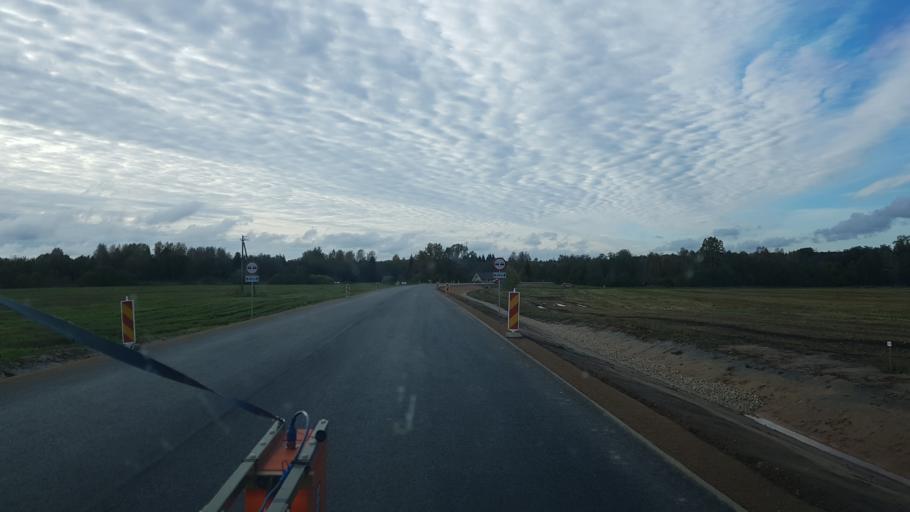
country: EE
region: Viljandimaa
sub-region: Abja vald
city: Abja-Paluoja
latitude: 58.3380
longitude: 25.3440
